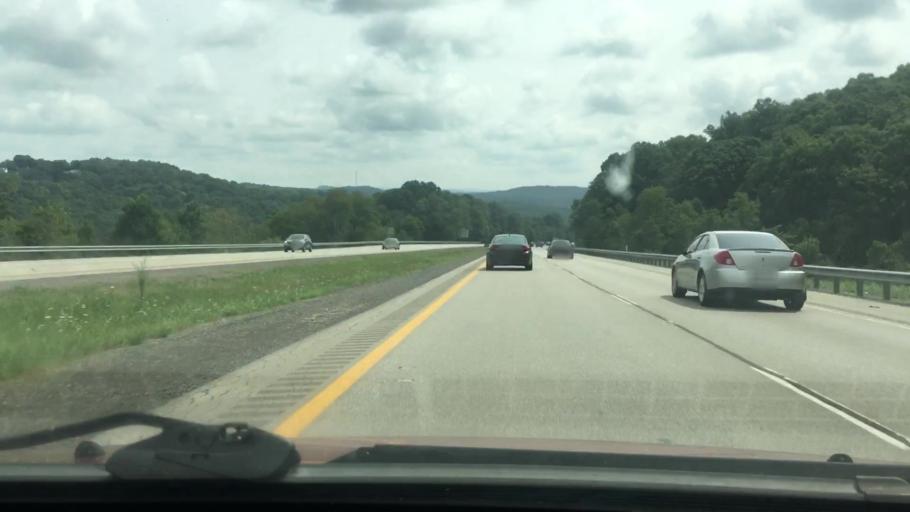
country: US
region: West Virginia
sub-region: Monongalia County
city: Cheat Lake
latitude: 39.6540
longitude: -79.7392
